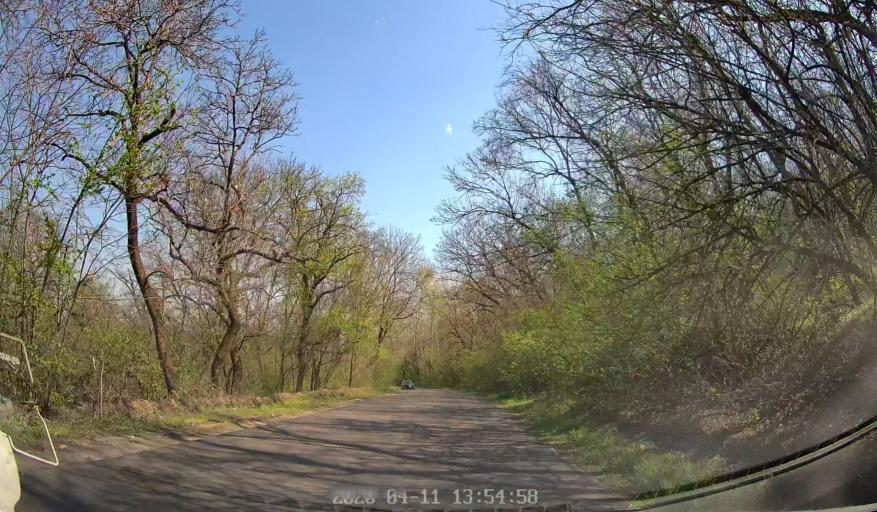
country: MD
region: Chisinau
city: Vadul lui Voda
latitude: 47.0729
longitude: 29.1077
